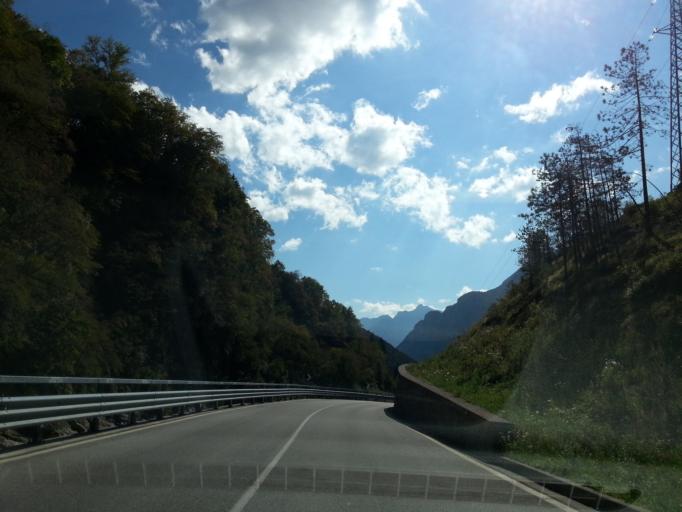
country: IT
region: Friuli Venezia Giulia
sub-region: Provincia di Udine
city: Moggio Udinese
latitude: 46.4685
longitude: 13.1906
